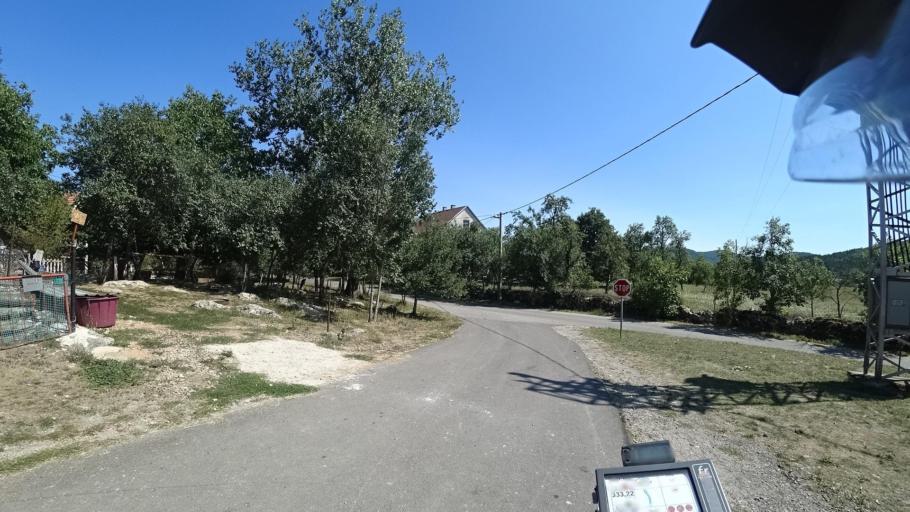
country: HR
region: Licko-Senjska
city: Popovaca
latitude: 44.7159
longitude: 15.2751
